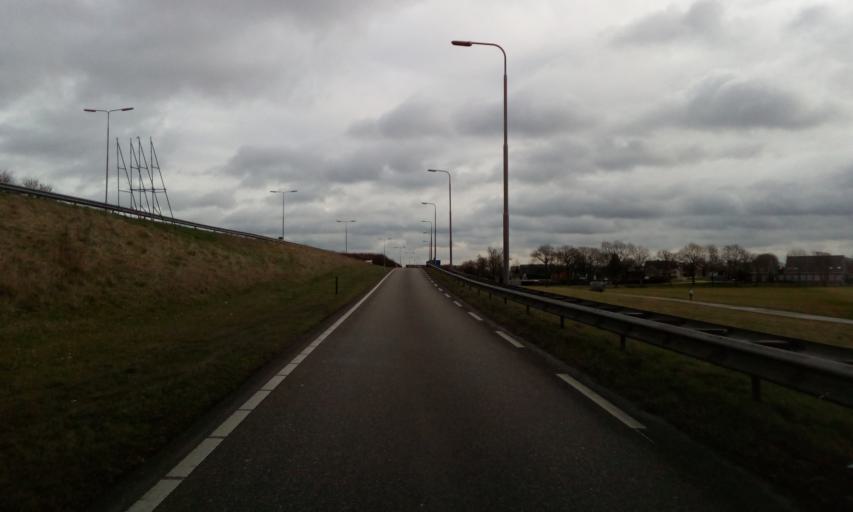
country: NL
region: South Holland
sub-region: Gemeente Hendrik-Ido-Ambacht
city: Hendrik-Ido-Ambacht
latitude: 51.8560
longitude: 4.6360
